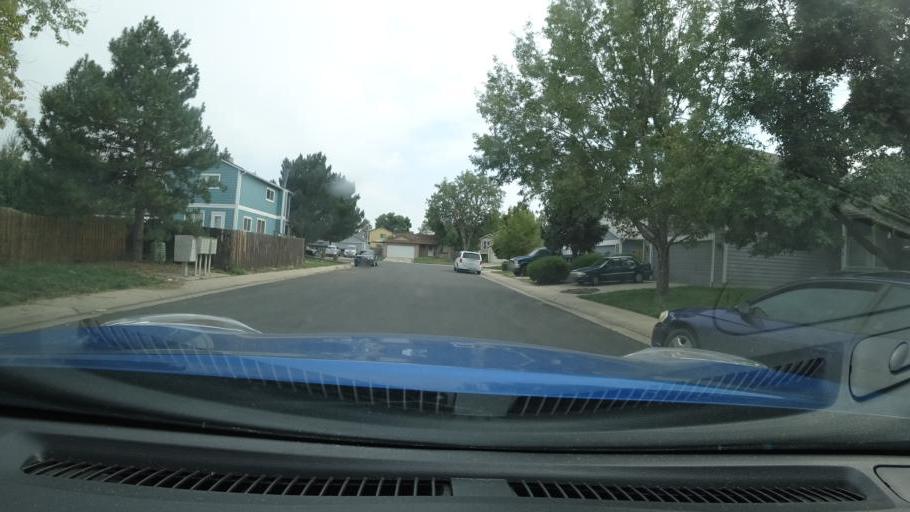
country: US
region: Colorado
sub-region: Adams County
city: Aurora
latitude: 39.7503
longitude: -104.7695
